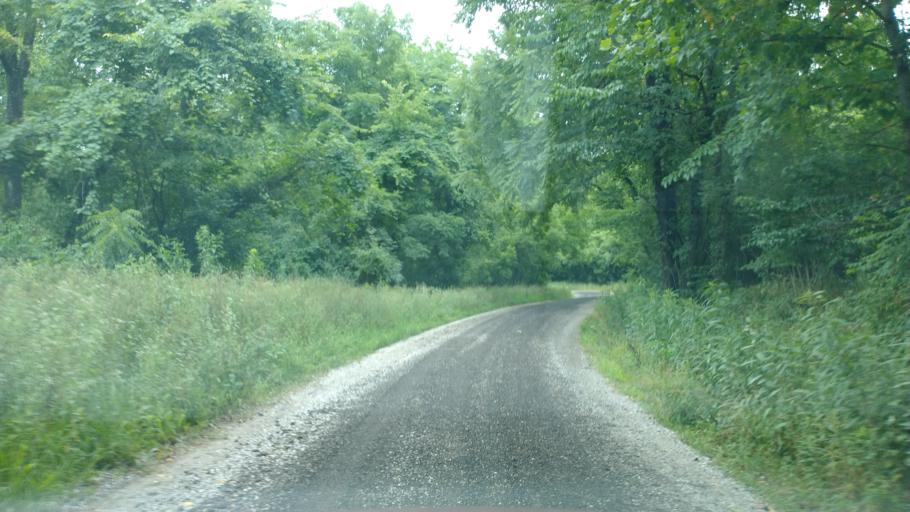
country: US
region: Ohio
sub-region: Meigs County
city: Middleport
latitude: 38.9295
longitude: -82.0648
